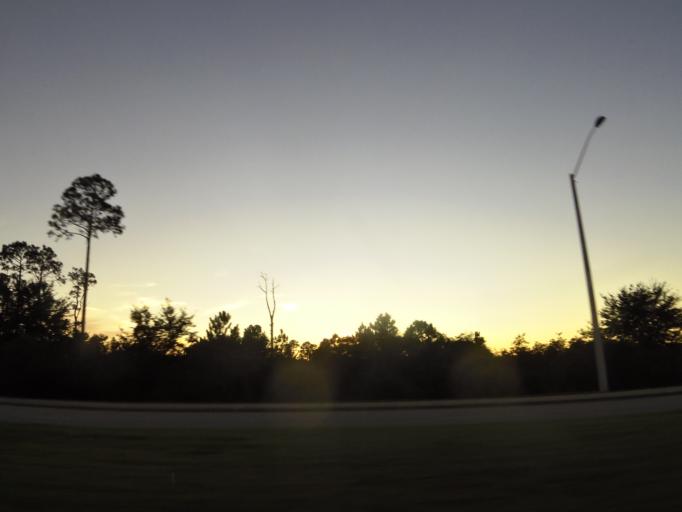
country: US
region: Florida
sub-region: Flagler County
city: Palm Coast
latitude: 29.5813
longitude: -81.2557
